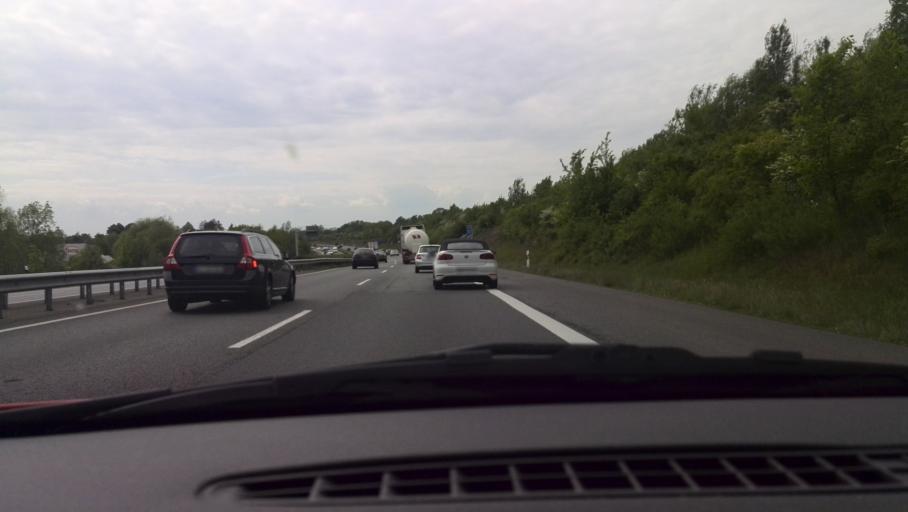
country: DE
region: Lower Saxony
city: Braunschweig
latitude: 52.2502
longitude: 10.5841
